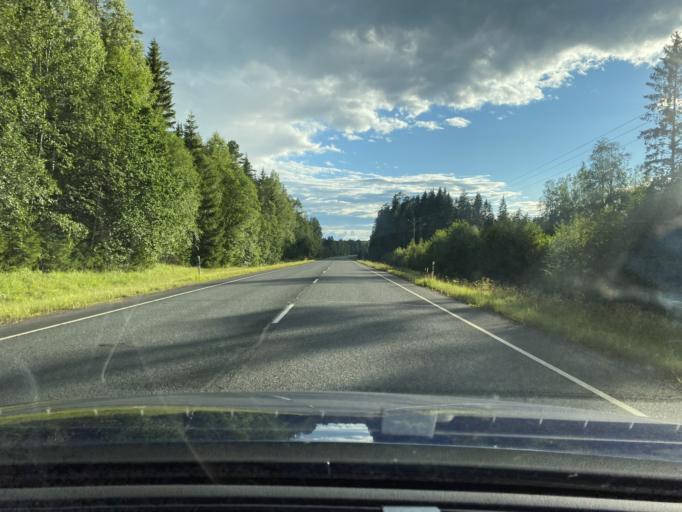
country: FI
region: Haeme
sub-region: Haemeenlinna
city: Renko
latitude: 60.8338
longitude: 24.0656
